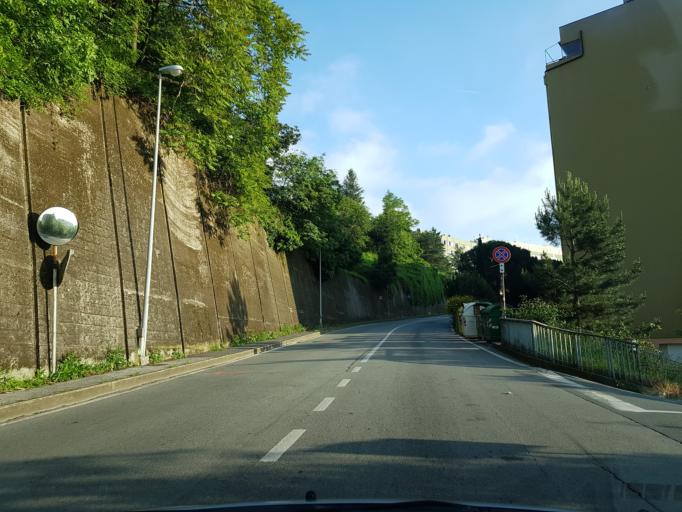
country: IT
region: Liguria
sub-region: Provincia di Genova
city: Genoa
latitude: 44.4519
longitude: 8.9093
